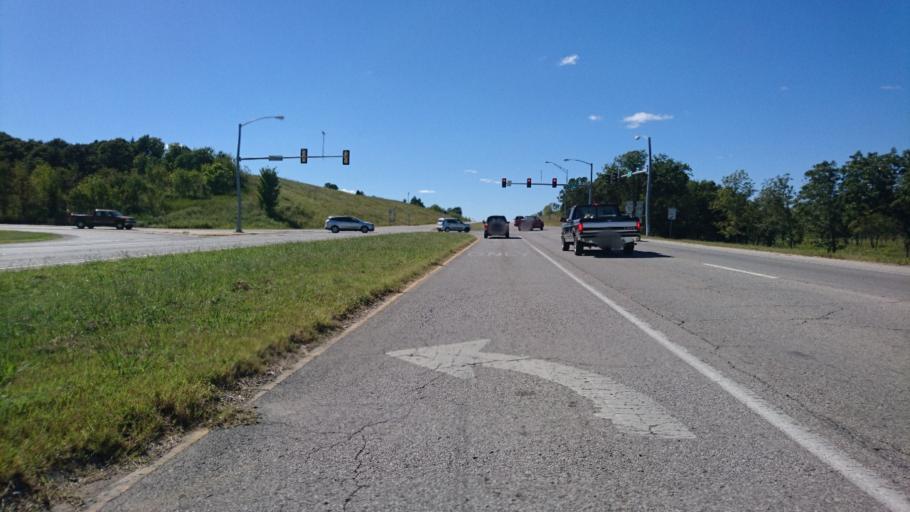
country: US
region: Oklahoma
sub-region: Creek County
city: Sapulpa
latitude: 35.9928
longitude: -96.1406
